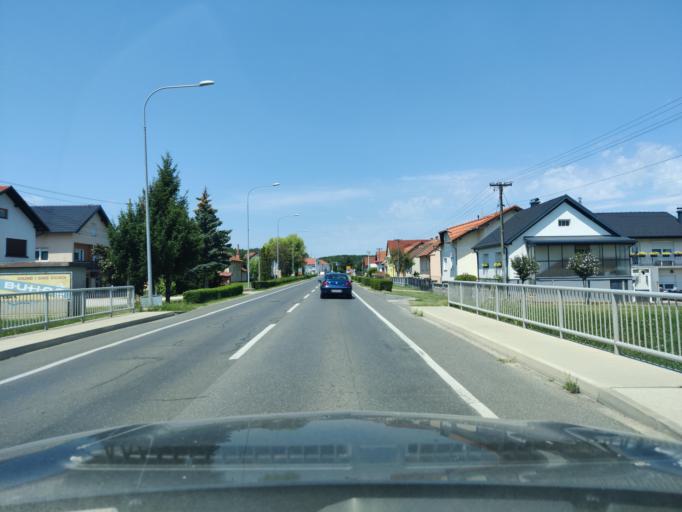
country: HR
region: Medimurska
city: Senkovec
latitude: 46.4016
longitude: 16.4236
